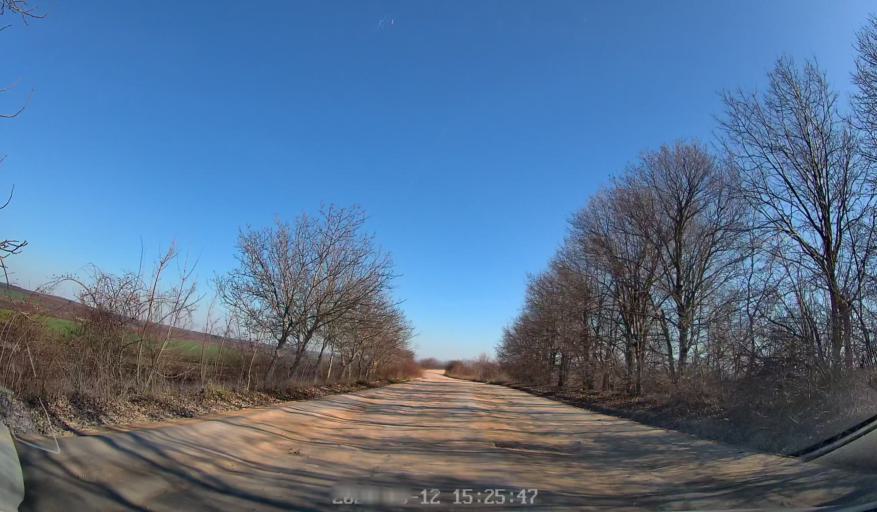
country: MD
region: Chisinau
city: Ciorescu
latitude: 47.1811
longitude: 28.9204
